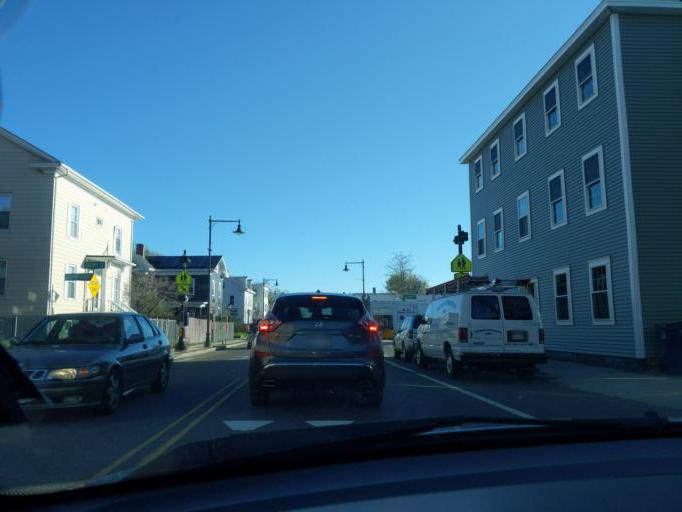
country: US
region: Massachusetts
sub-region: Essex County
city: Salem
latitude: 42.5306
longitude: -70.8892
